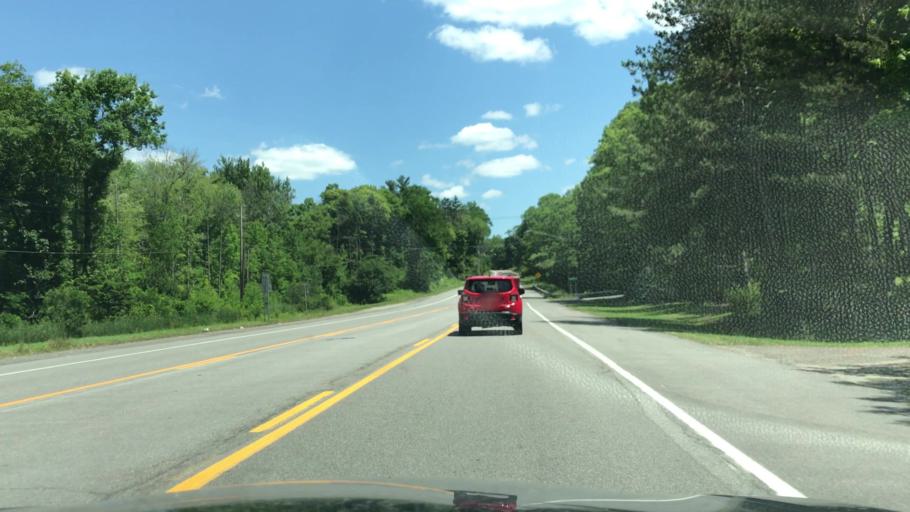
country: US
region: New York
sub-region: Erie County
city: East Aurora
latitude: 42.7674
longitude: -78.5900
